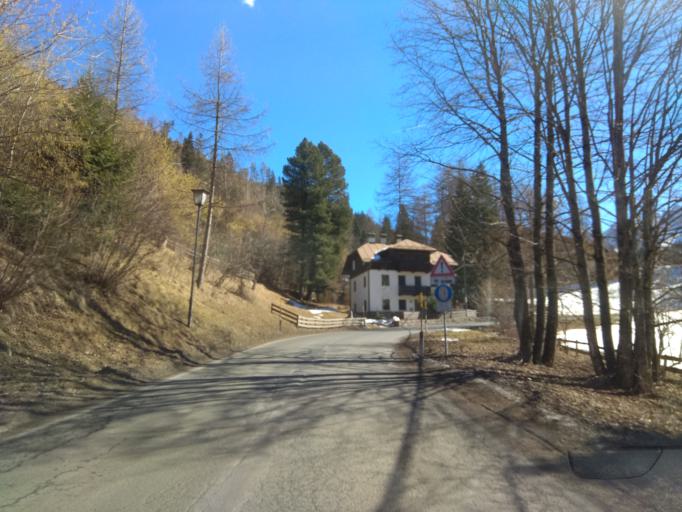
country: IT
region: Trentino-Alto Adige
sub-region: Bolzano
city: Nova Levante
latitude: 46.4217
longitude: 11.5579
